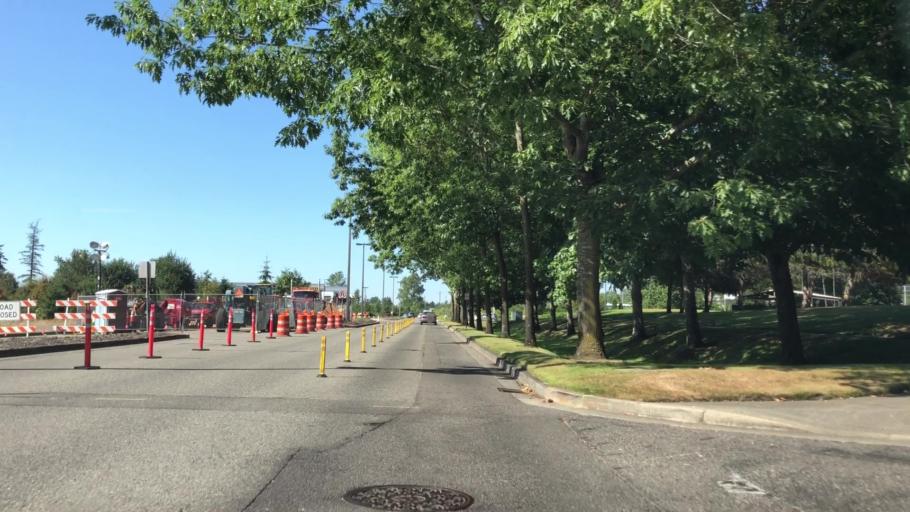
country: US
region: Washington
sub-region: Snohomish County
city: North Creek
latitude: 47.8008
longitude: -122.2062
